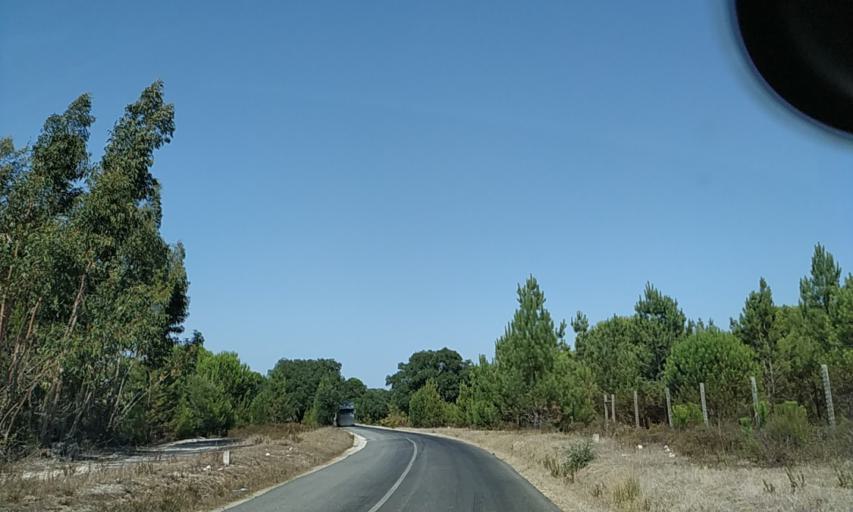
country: PT
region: Santarem
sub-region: Benavente
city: Poceirao
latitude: 38.7231
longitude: -8.7073
